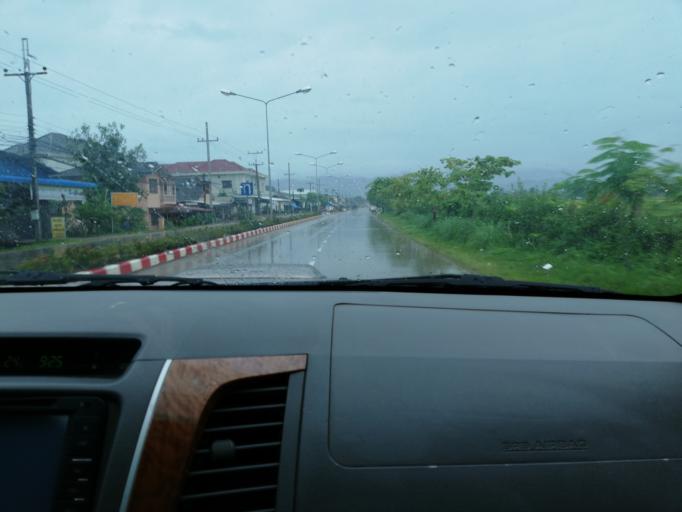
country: LA
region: Loungnamtha
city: Louang Namtha
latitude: 20.9545
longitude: 101.4038
